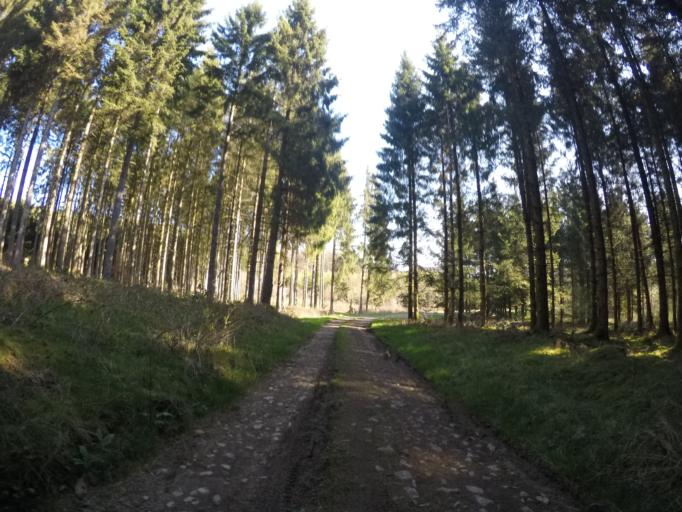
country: BE
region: Wallonia
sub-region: Province du Luxembourg
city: Leglise
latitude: 49.7846
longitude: 5.5875
